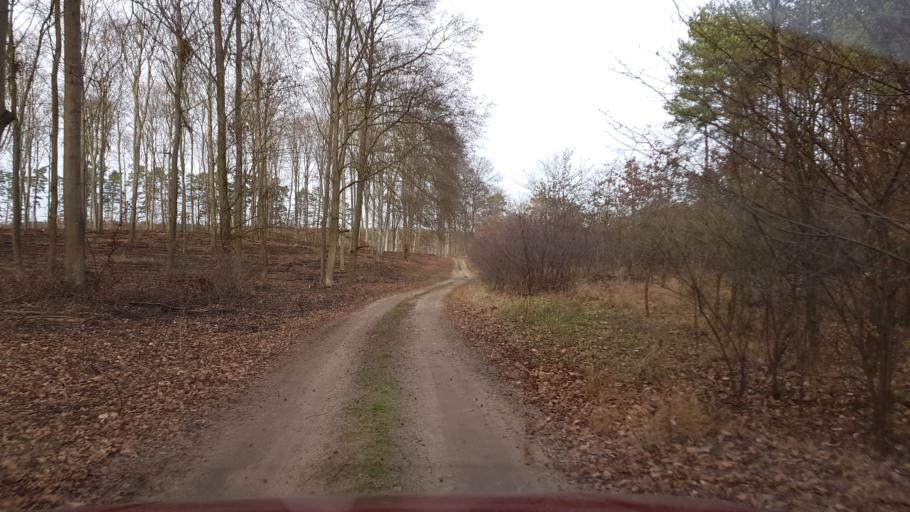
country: PL
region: Lubusz
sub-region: Powiat strzelecko-drezdenecki
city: Strzelce Krajenskie
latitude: 52.9159
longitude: 15.4119
